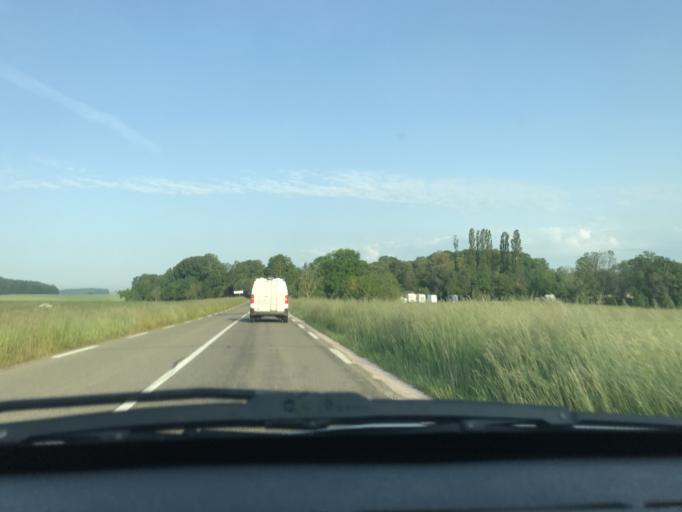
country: FR
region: Lorraine
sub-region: Departement de la Moselle
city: Vic-sur-Seille
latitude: 48.7802
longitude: 6.4951
